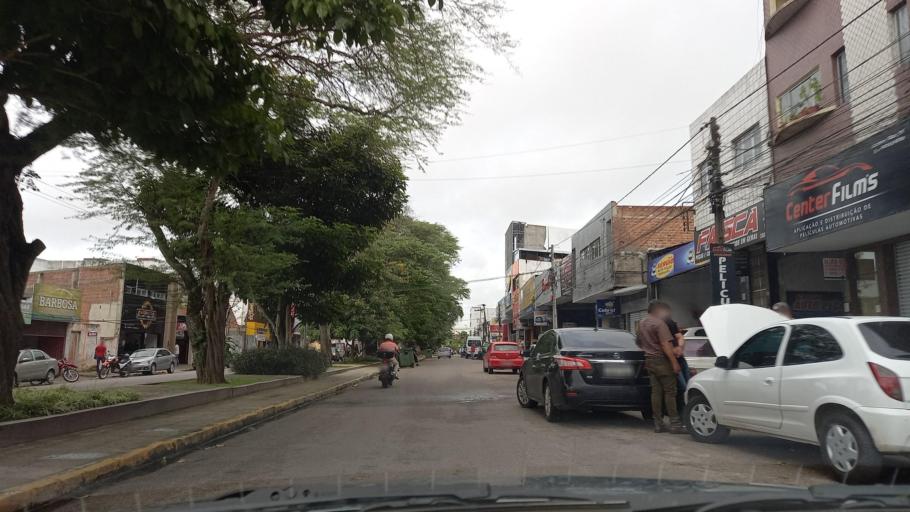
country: BR
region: Pernambuco
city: Garanhuns
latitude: -8.8842
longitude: -36.4886
